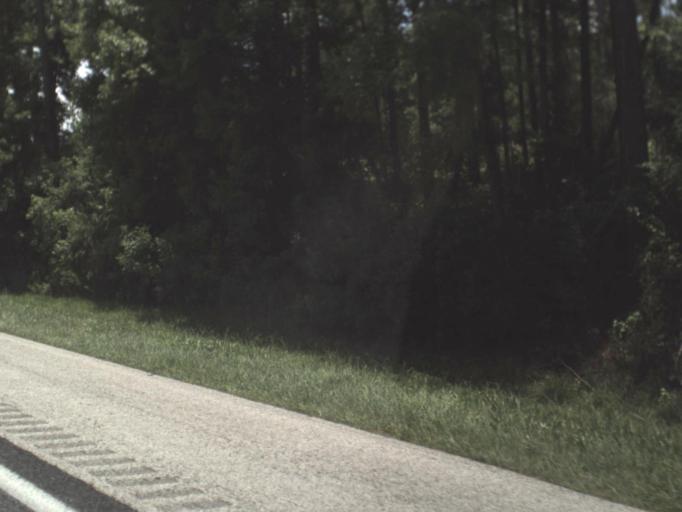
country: US
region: Florida
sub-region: Alachua County
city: Alachua
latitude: 29.7135
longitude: -82.4646
